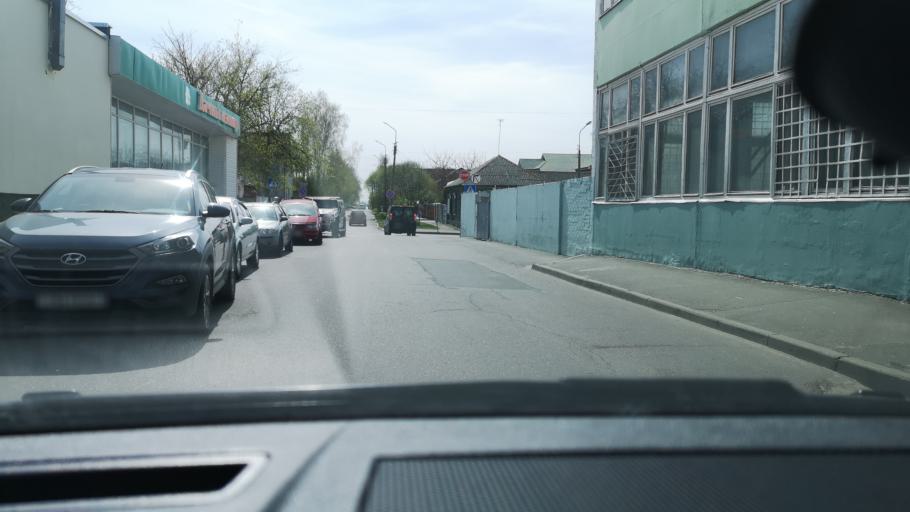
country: BY
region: Gomel
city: Gomel
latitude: 52.4205
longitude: 31.0086
